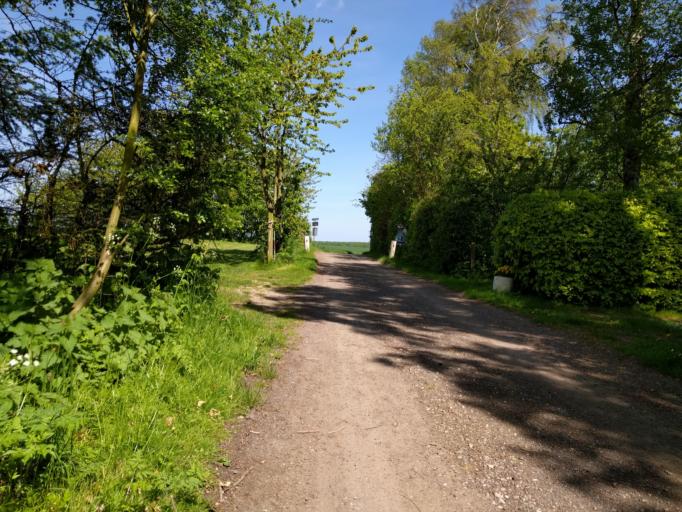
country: DK
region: Zealand
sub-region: Guldborgsund Kommune
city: Stubbekobing
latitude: 54.7461
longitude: 12.0320
